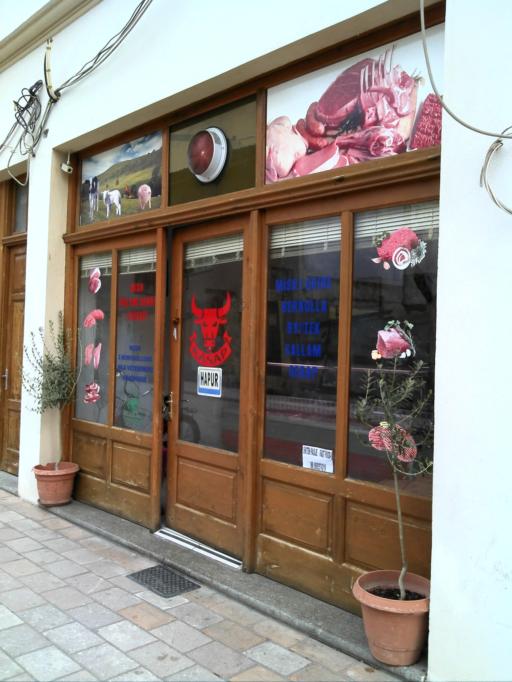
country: AL
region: Shkoder
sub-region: Rrethi i Shkodres
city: Shkoder
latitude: 42.0658
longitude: 19.5188
